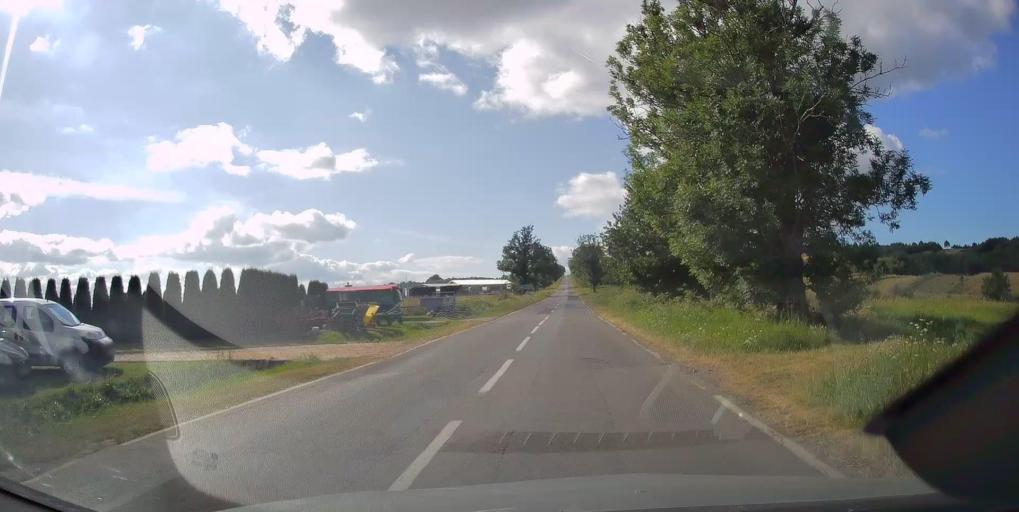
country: PL
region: Swietokrzyskie
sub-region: Powiat skarzyski
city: Suchedniow
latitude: 50.9818
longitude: 20.8752
